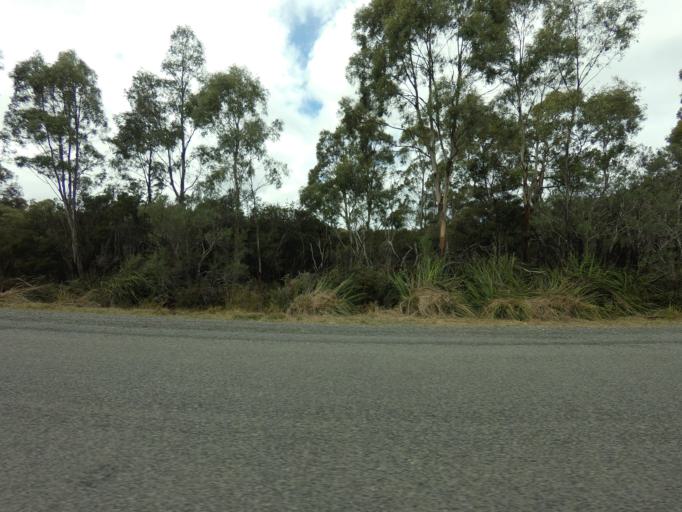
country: AU
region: Tasmania
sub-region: Huon Valley
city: Geeveston
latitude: -43.4228
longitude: 146.9048
